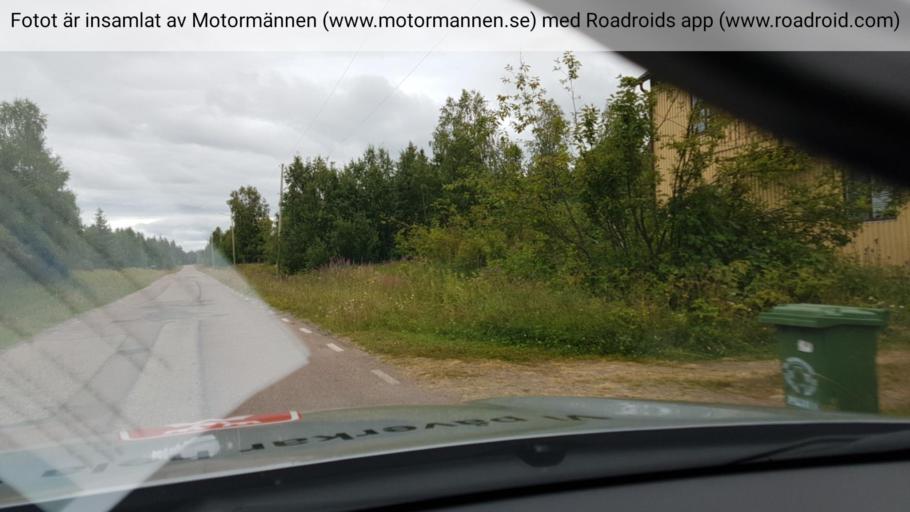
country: SE
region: Norrbotten
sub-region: Pajala Kommun
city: Pajala
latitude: 66.9606
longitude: 22.9482
